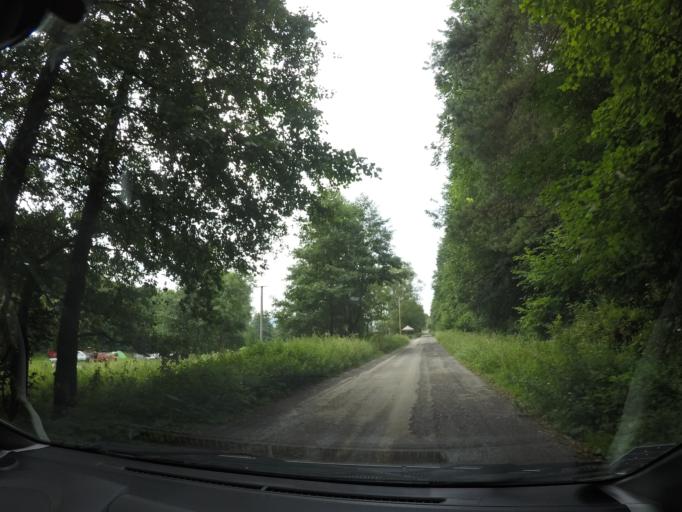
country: SK
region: Nitriansky
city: Bojnice
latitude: 48.9080
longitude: 18.6022
